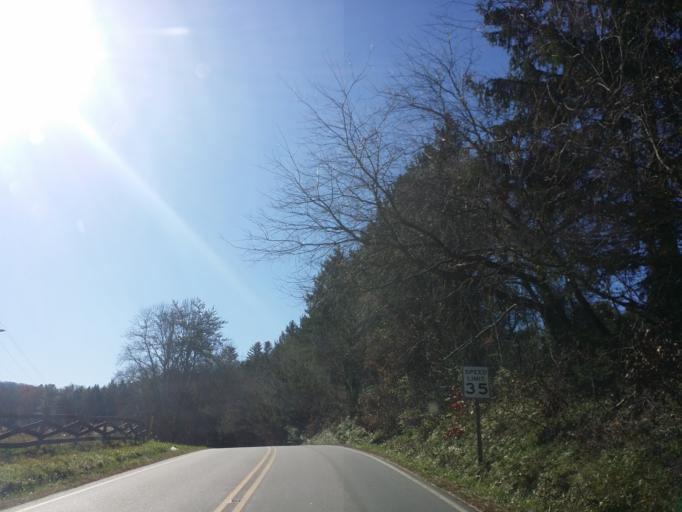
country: US
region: North Carolina
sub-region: Buncombe County
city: Swannanoa
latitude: 35.6042
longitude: -82.4447
